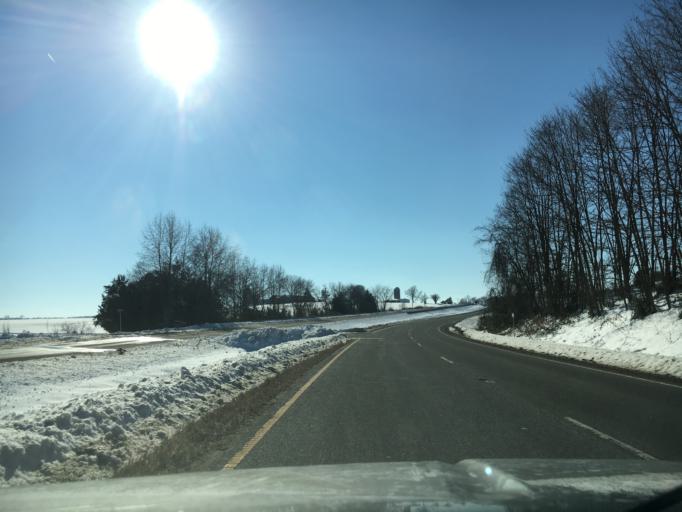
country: US
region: Virginia
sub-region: Nottoway County
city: Crewe
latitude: 37.2735
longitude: -78.1207
